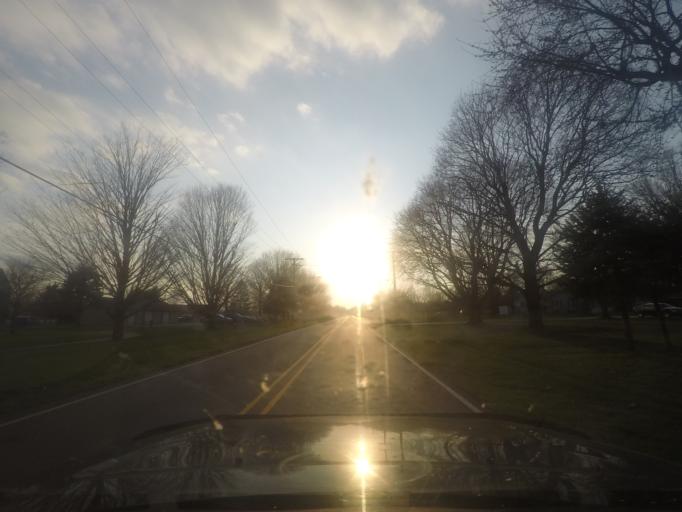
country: US
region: Indiana
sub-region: LaPorte County
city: LaPorte
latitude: 41.5914
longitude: -86.7141
